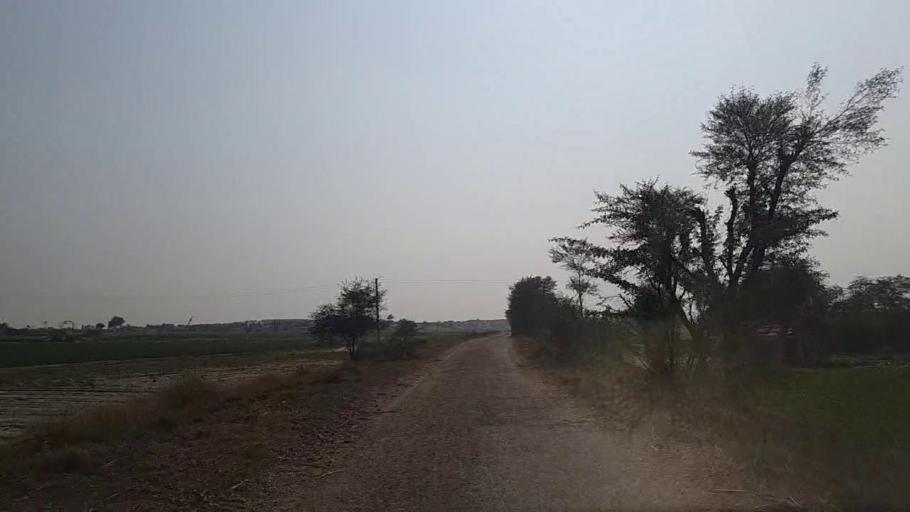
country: PK
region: Sindh
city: Jam Sahib
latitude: 26.4407
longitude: 68.5232
